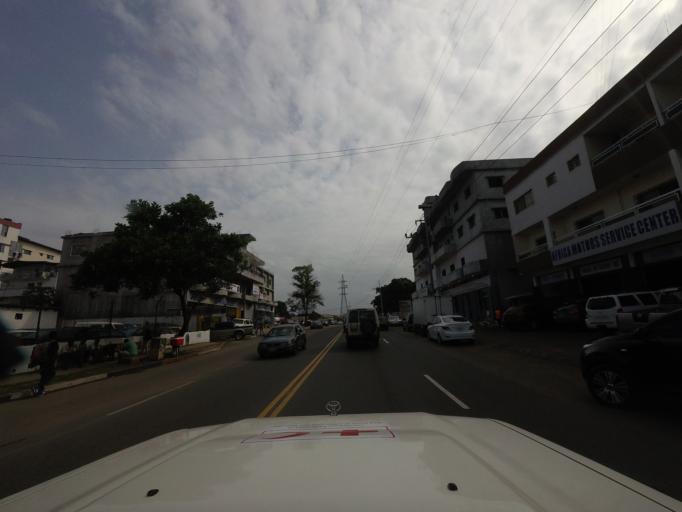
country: LR
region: Montserrado
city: Monrovia
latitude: 6.3127
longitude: -10.7982
